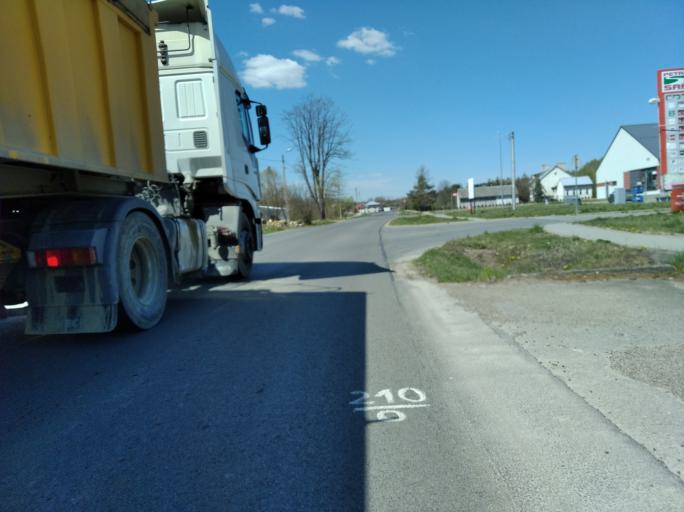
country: PL
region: Subcarpathian Voivodeship
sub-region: Powiat brzozowski
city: Dydnia
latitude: 49.6877
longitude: 22.1677
